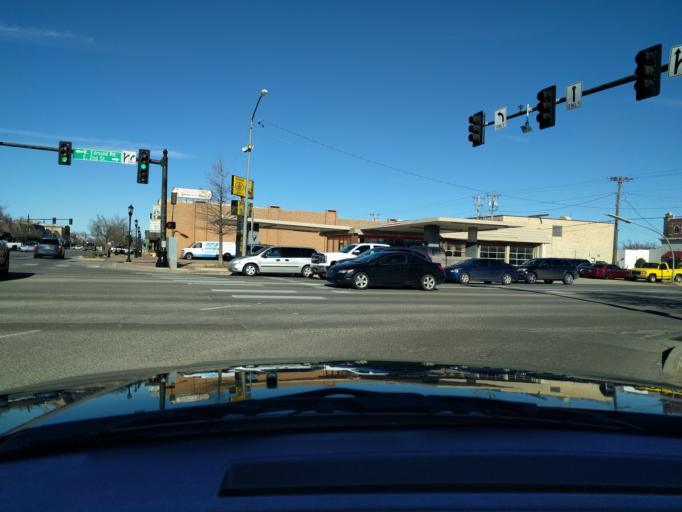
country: US
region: Oklahoma
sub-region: Oklahoma County
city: Edmond
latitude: 35.6531
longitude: -97.4814
